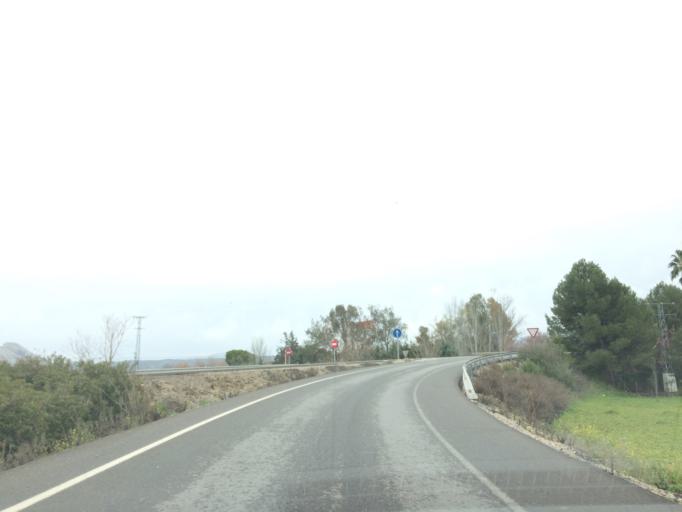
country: ES
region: Andalusia
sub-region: Provincia de Malaga
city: Antequera
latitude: 37.0741
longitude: -4.5667
